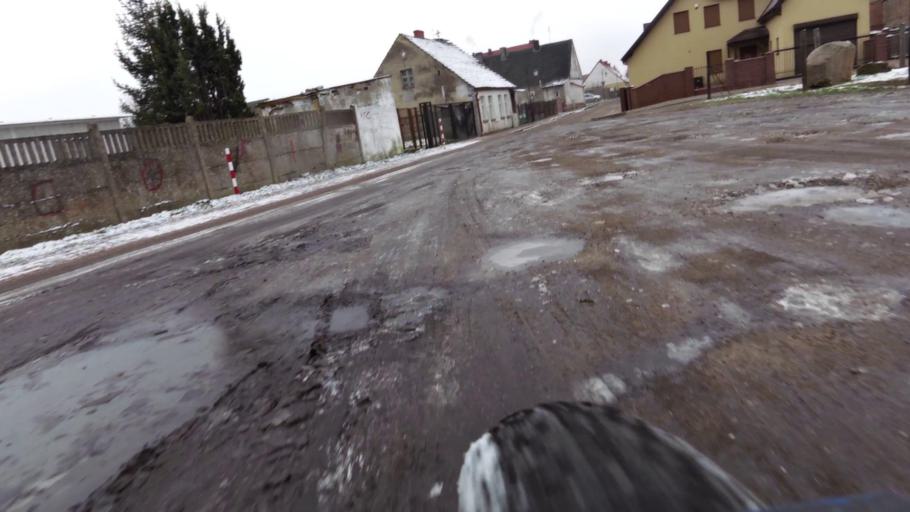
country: PL
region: West Pomeranian Voivodeship
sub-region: Powiat walecki
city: Miroslawiec
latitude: 53.3401
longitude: 16.0948
